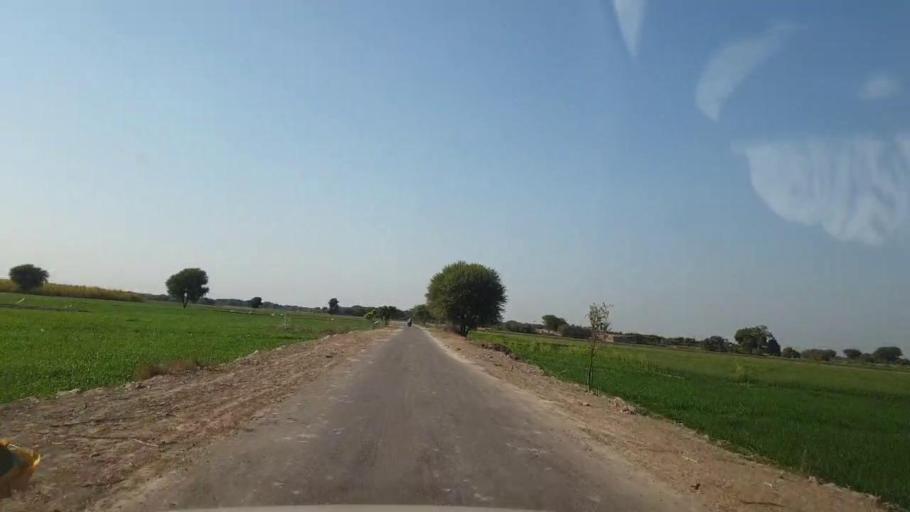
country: PK
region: Sindh
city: Tando Allahyar
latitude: 25.4848
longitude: 68.6587
